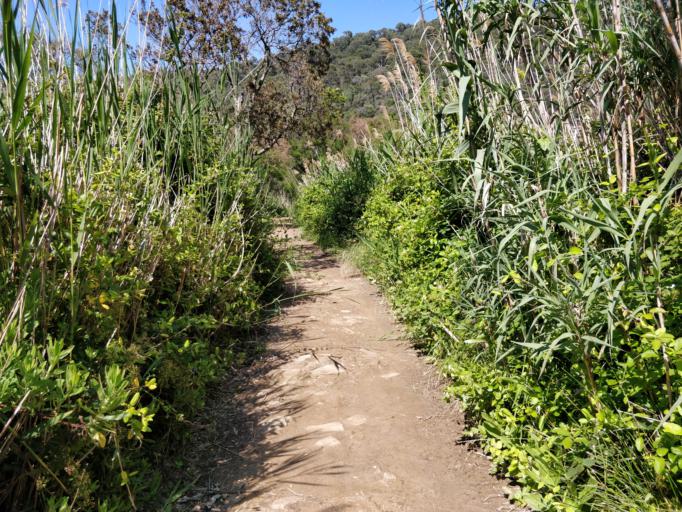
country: FR
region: Provence-Alpes-Cote d'Azur
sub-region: Departement du Var
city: Le Lavandou
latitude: 43.0064
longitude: 6.3830
